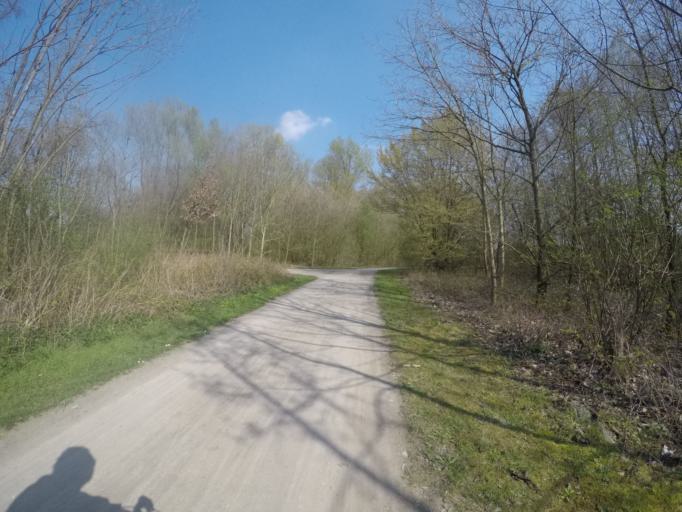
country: DE
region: North Rhine-Westphalia
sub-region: Regierungsbezirk Detmold
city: Bielefeld
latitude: 52.0363
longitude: 8.5977
